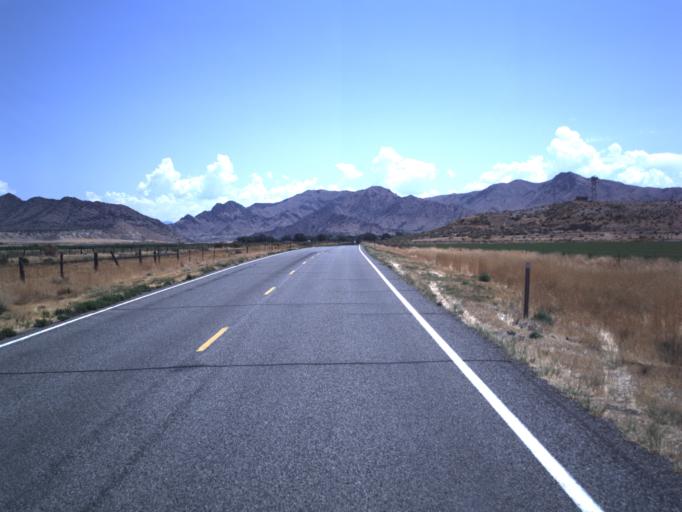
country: US
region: Utah
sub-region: Millard County
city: Delta
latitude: 39.5332
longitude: -112.3204
